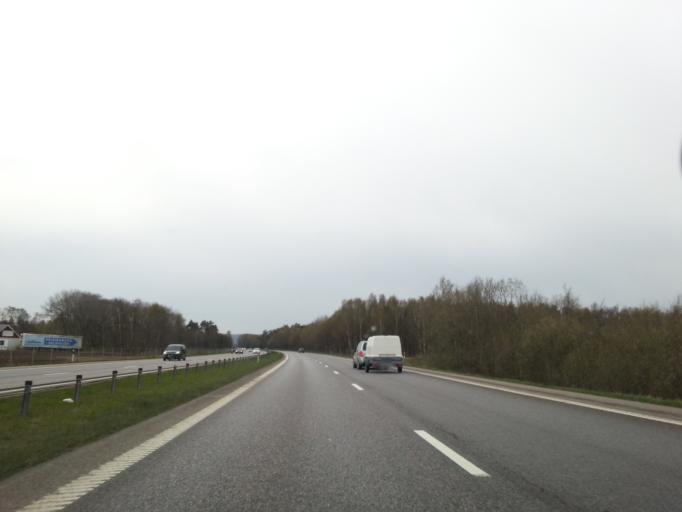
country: SE
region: Halland
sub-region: Laholms Kommun
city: Mellbystrand
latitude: 56.4716
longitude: 12.9421
